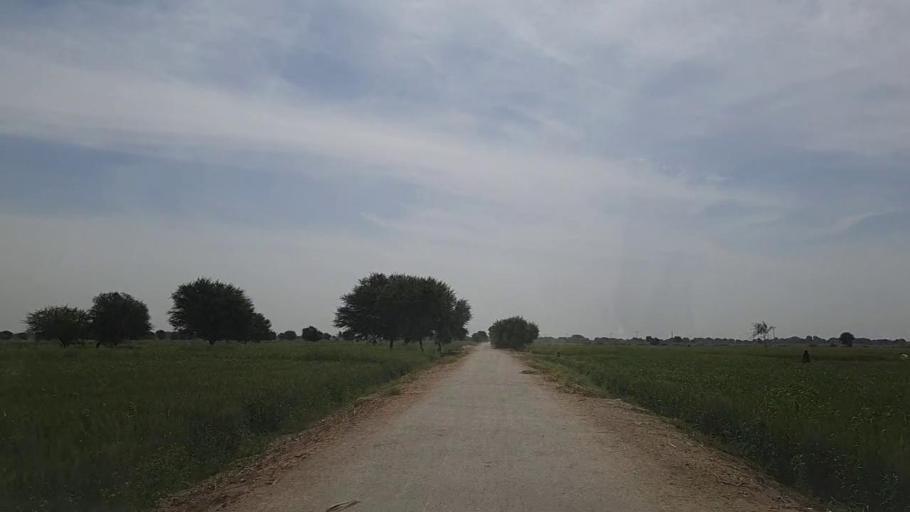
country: PK
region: Sindh
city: Samaro
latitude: 25.2748
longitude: 69.4536
